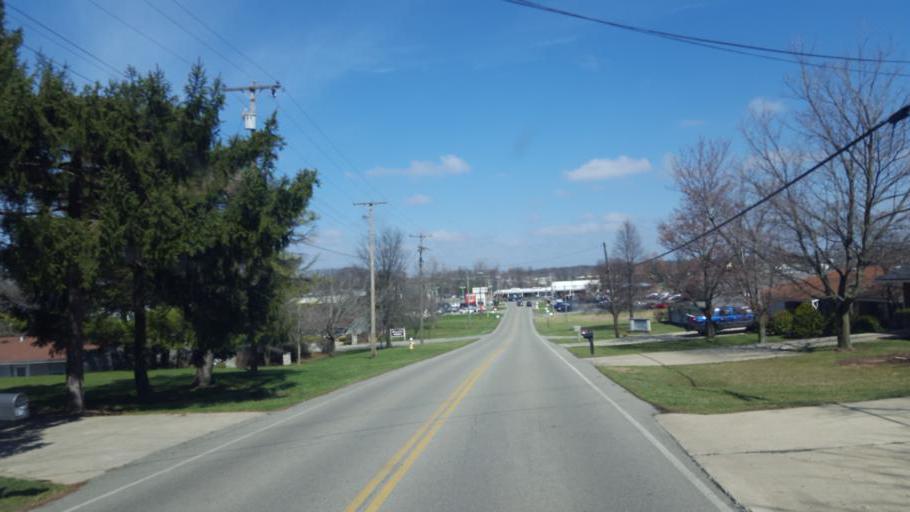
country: US
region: Ohio
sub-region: Richland County
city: Ontario
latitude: 40.7653
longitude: -82.5637
